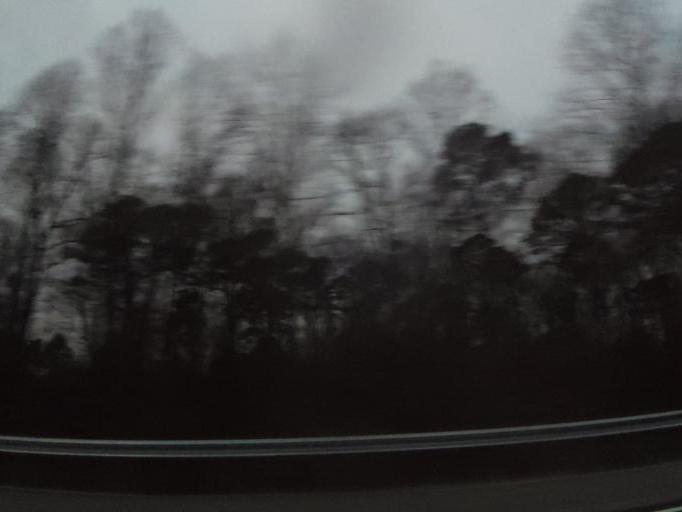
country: US
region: Alabama
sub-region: Morgan County
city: Falkville
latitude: 34.2719
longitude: -86.8988
